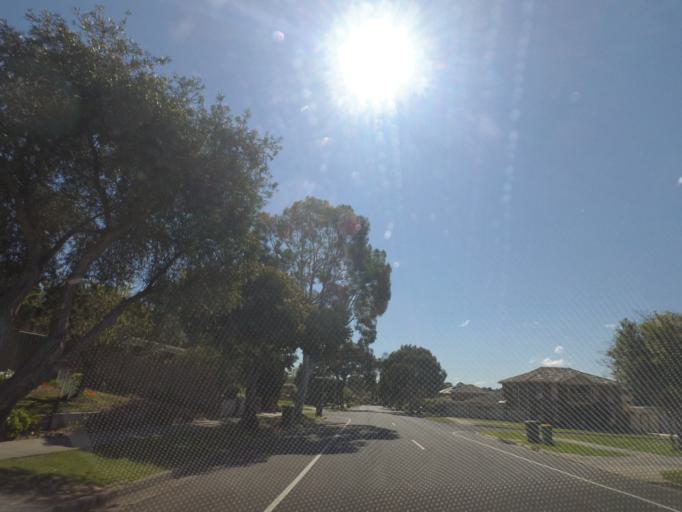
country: AU
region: Victoria
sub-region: Knox
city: Wantirna South
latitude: -37.8832
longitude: 145.2238
